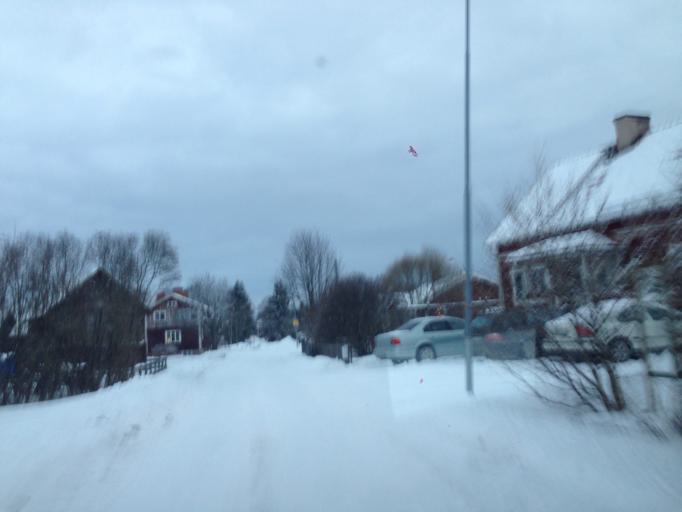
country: SE
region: Dalarna
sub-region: Mora Kommun
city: Mora
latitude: 61.0054
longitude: 14.5875
